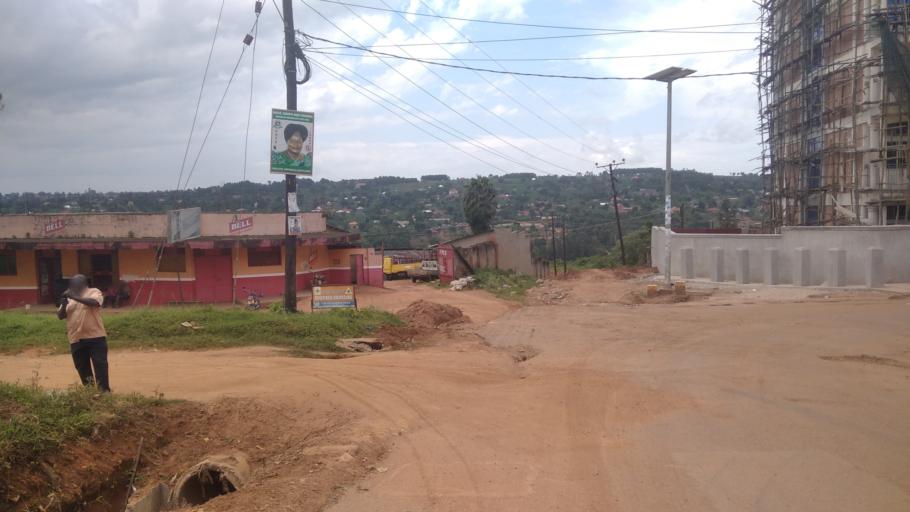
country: UG
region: Central Region
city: Masaka
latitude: -0.3402
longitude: 31.7398
